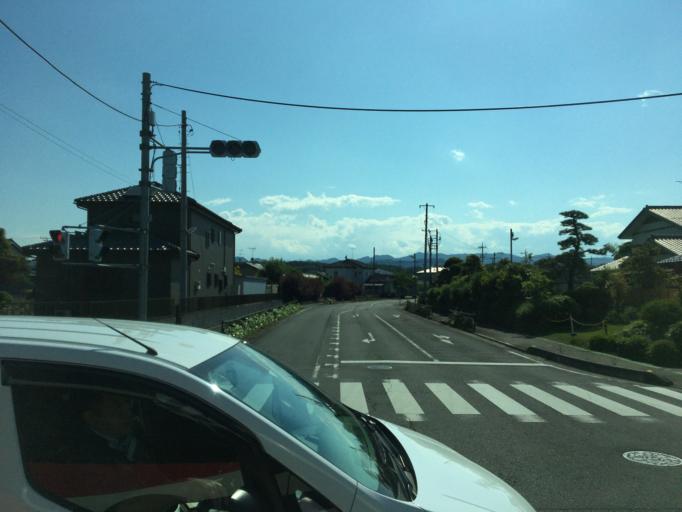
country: JP
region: Saitama
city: Sakado
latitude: 35.9683
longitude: 139.3428
